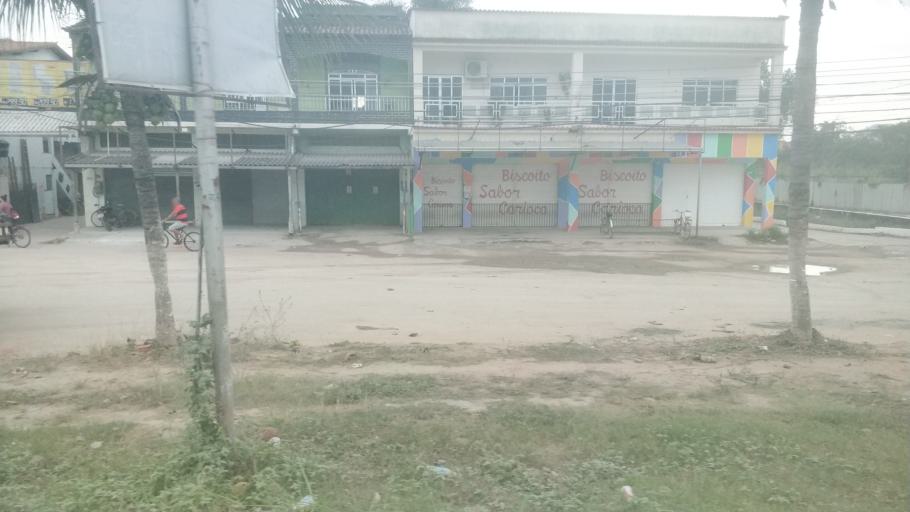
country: BR
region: Rio de Janeiro
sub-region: Seropedica
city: Seropedica
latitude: -22.8014
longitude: -43.6430
